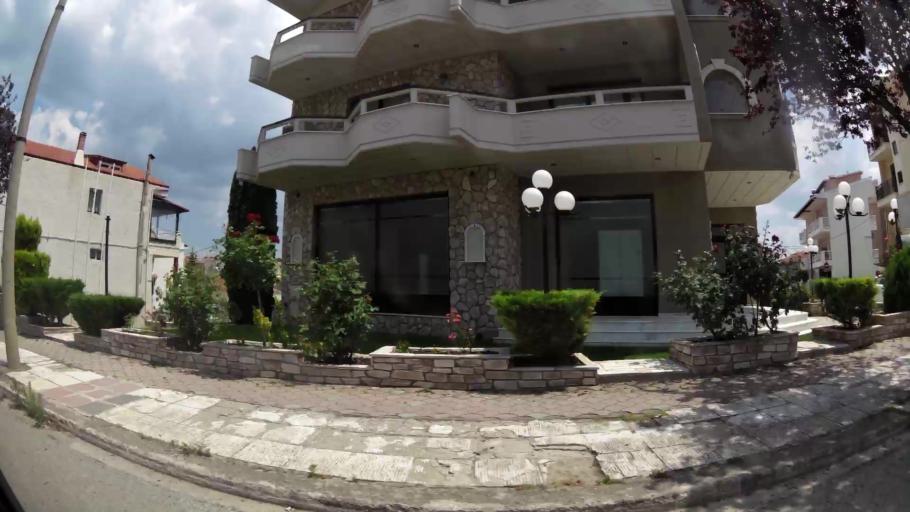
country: GR
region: West Macedonia
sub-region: Nomos Kozanis
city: Kozani
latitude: 40.2911
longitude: 21.7823
